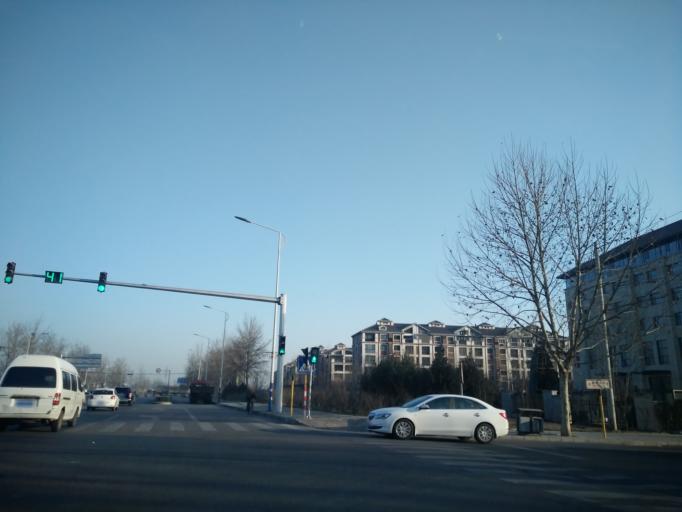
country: CN
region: Beijing
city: Weishanzhuang
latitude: 39.6665
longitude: 116.4080
